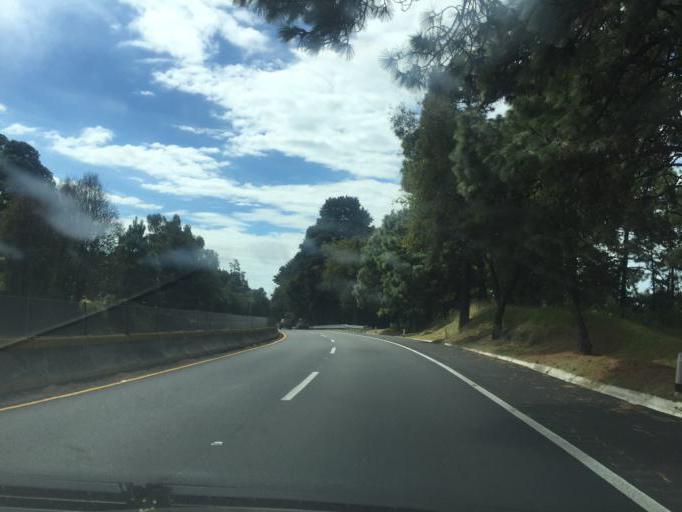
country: MX
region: Morelos
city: Tres Marias
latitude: 19.0631
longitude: -99.2388
